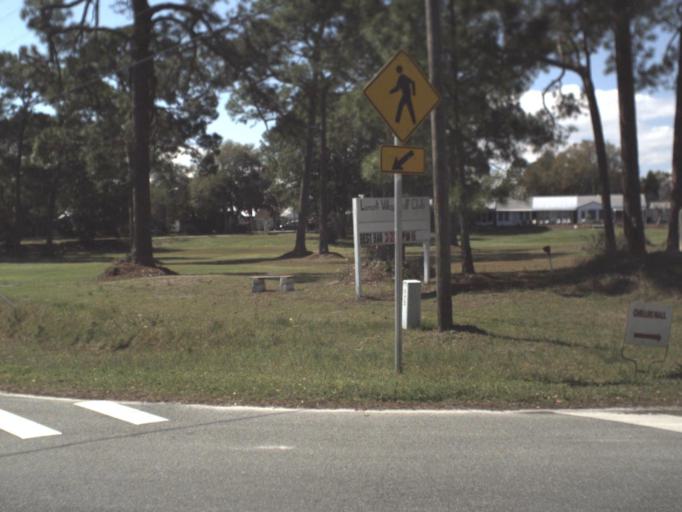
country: US
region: Florida
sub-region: Franklin County
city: Carrabelle
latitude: 29.8829
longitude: -84.5916
